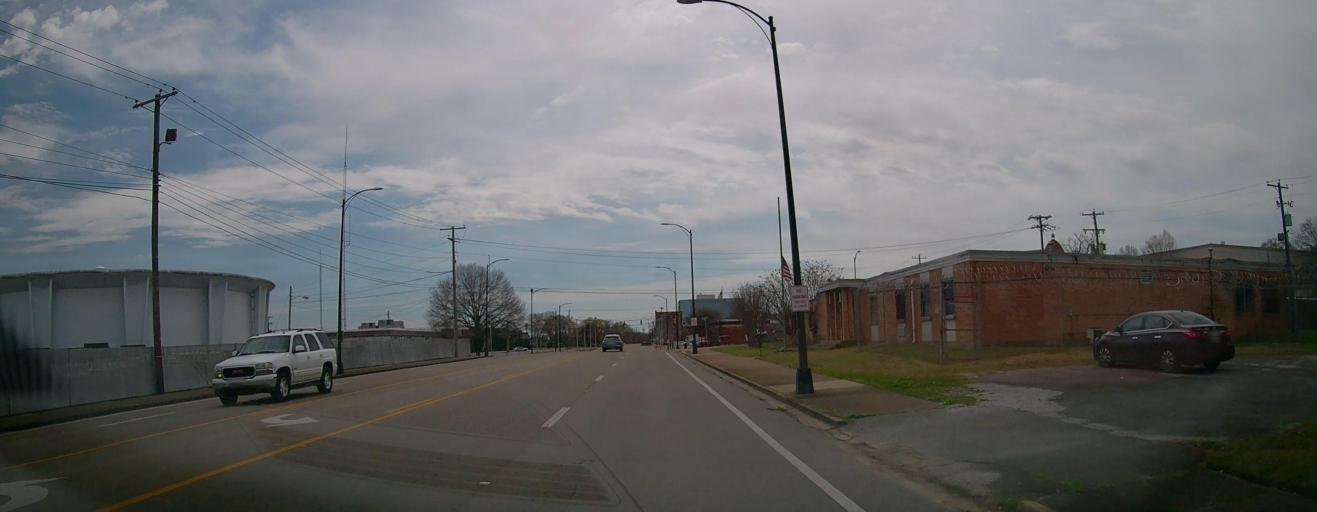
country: US
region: Mississippi
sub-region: Lee County
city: Tupelo
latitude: 34.2615
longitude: -88.7034
